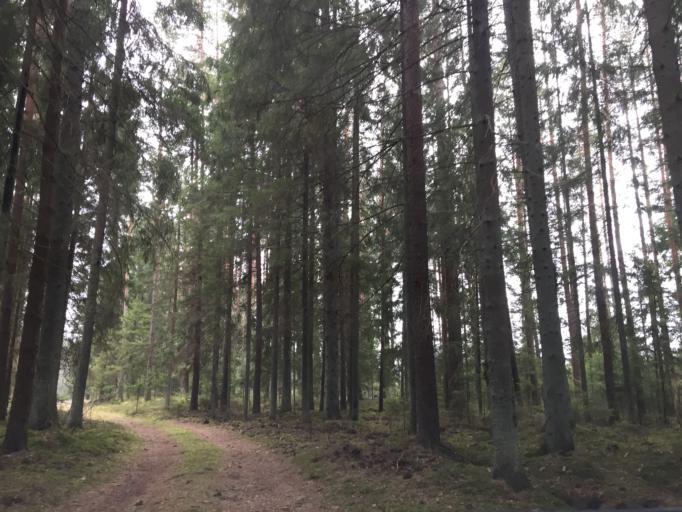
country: LV
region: Kekava
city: Kekava
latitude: 56.7662
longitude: 24.1568
